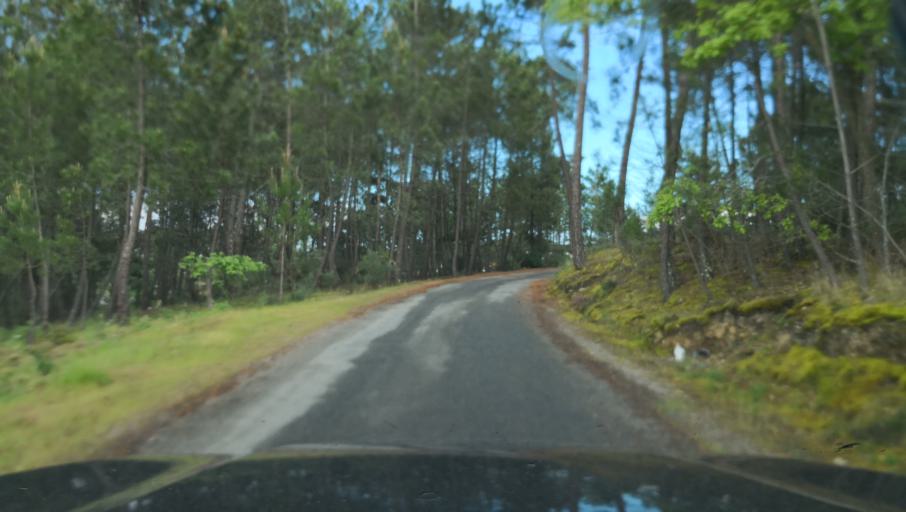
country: PT
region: Vila Real
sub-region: Vila Real
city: Vila Real
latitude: 41.3222
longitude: -7.6920
